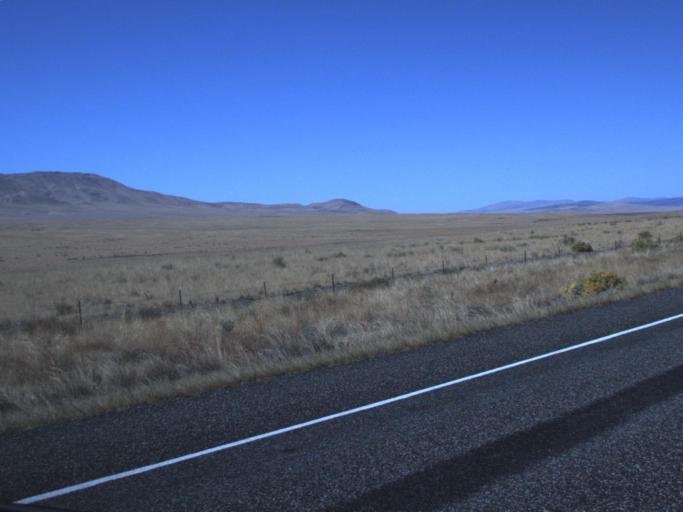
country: US
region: Washington
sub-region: Benton County
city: West Richland
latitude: 46.4222
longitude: -119.4673
